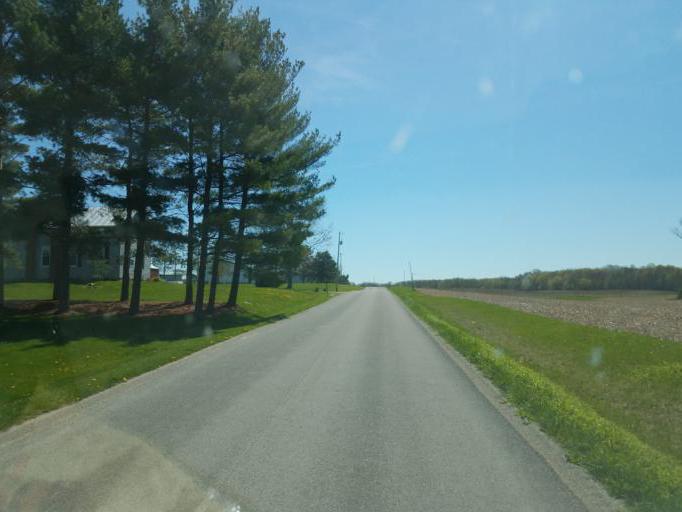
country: US
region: Ohio
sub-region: Morrow County
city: Mount Gilead
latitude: 40.5987
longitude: -82.7921
